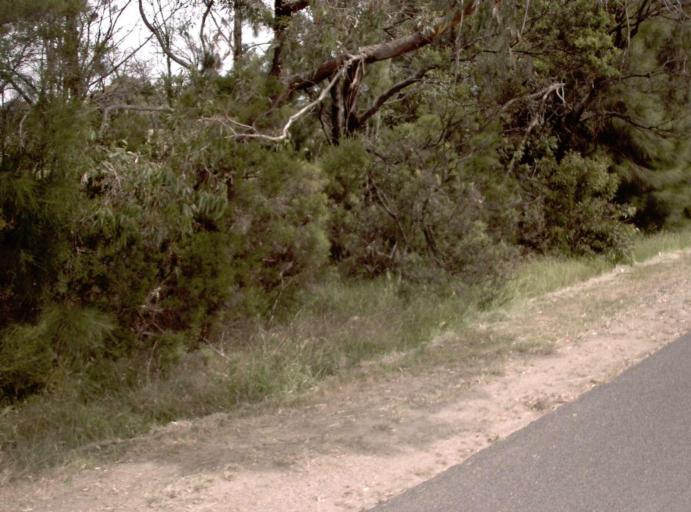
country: AU
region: Victoria
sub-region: Mornington Peninsula
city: Moorooduc
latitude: -38.2281
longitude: 145.0962
